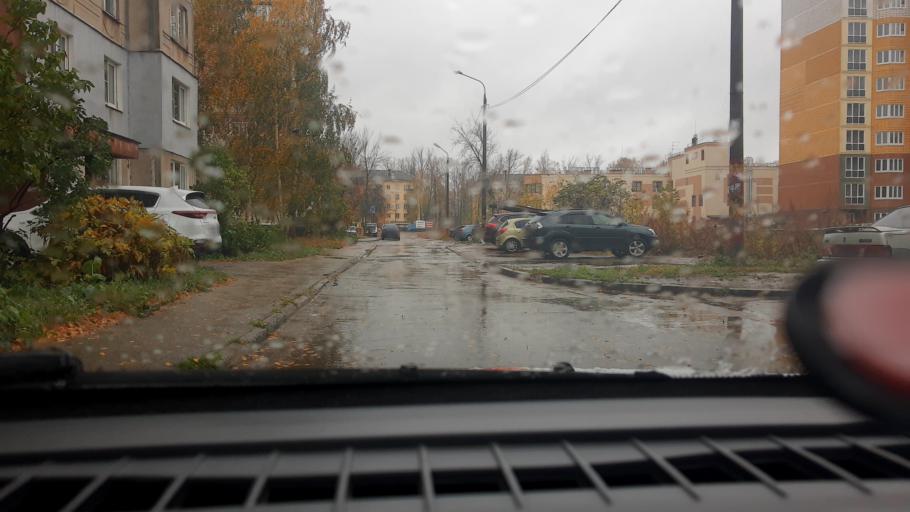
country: RU
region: Nizjnij Novgorod
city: Kstovo
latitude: 56.1539
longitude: 44.2074
